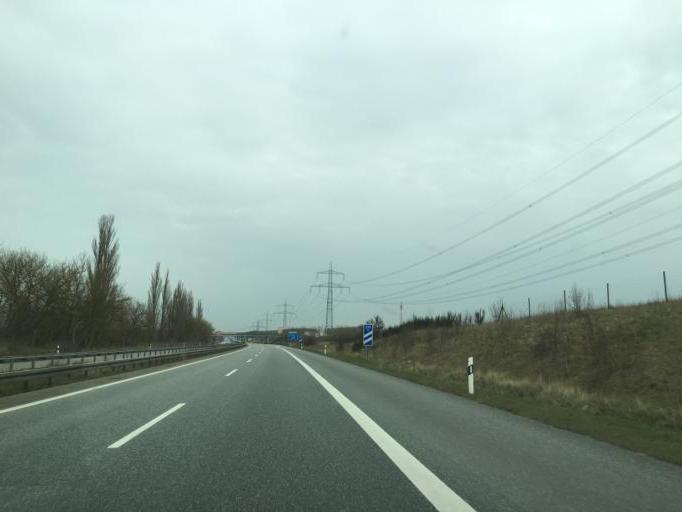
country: DE
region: Mecklenburg-Vorpommern
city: Kavelstorf
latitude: 54.0073
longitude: 12.2035
